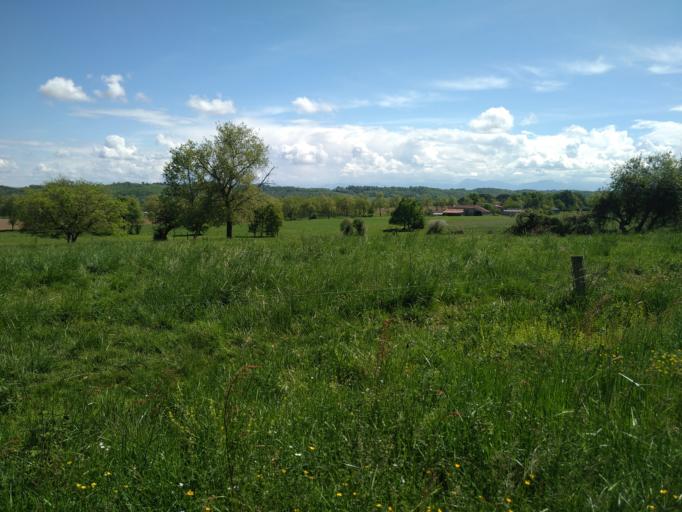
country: FR
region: Midi-Pyrenees
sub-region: Departement de la Haute-Garonne
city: Boulogne-sur-Gesse
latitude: 43.3022
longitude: 0.6681
